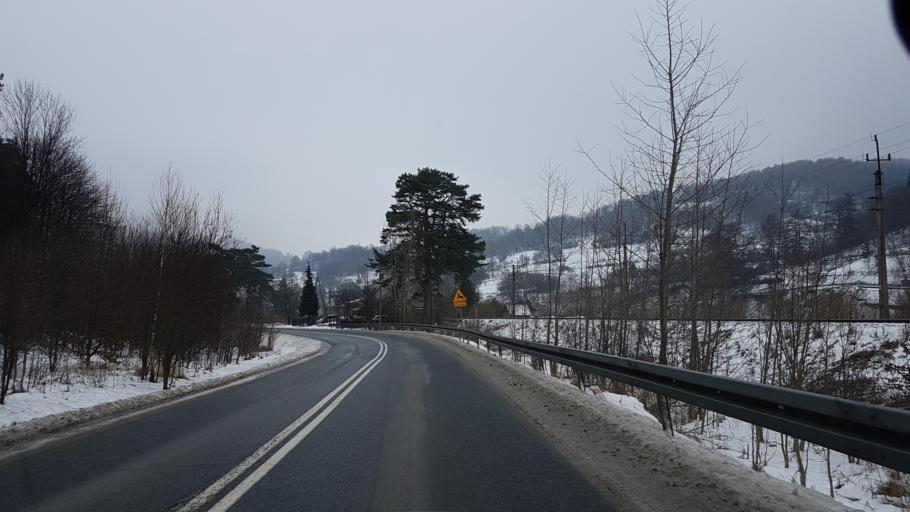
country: PL
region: Lesser Poland Voivodeship
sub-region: Powiat nowosadecki
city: Piwniczna-Zdroj
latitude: 49.4166
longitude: 20.7277
